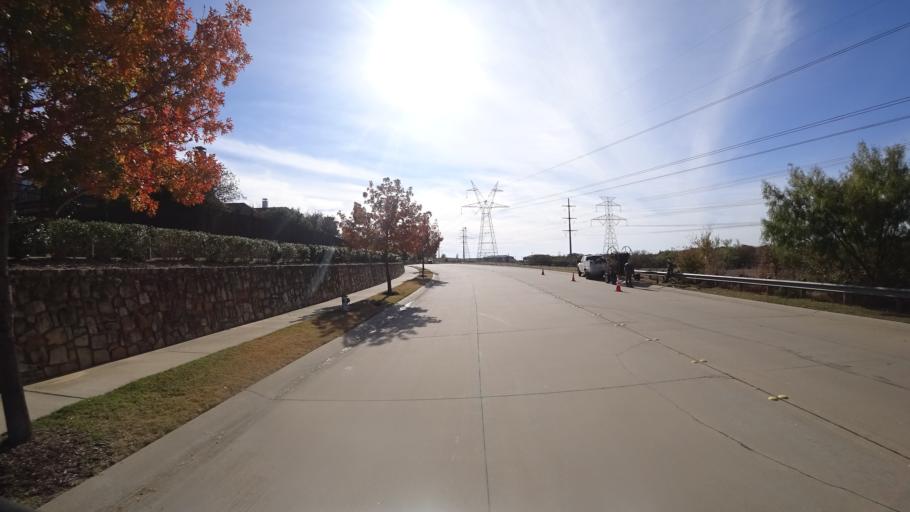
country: US
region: Texas
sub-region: Denton County
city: The Colony
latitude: 33.0295
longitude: -96.9132
